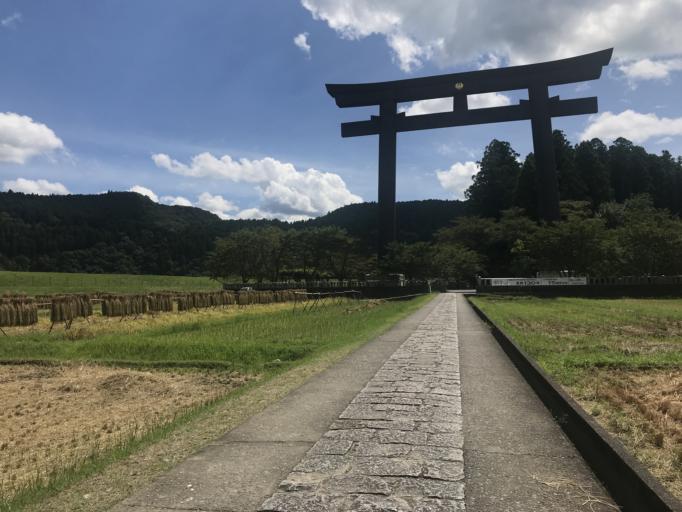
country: JP
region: Wakayama
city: Shingu
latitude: 33.8366
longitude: 135.7756
